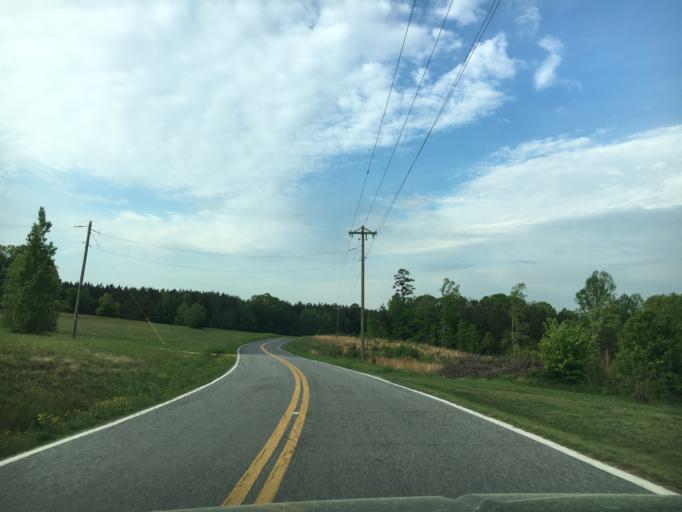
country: US
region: Virginia
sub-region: Halifax County
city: Halifax
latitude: 36.8948
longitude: -78.8298
